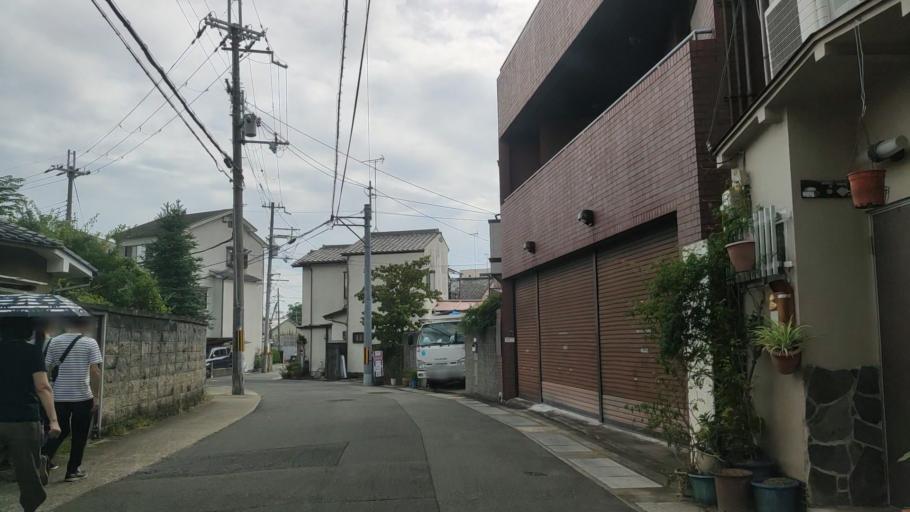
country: JP
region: Kyoto
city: Muko
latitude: 35.0154
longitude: 135.6824
